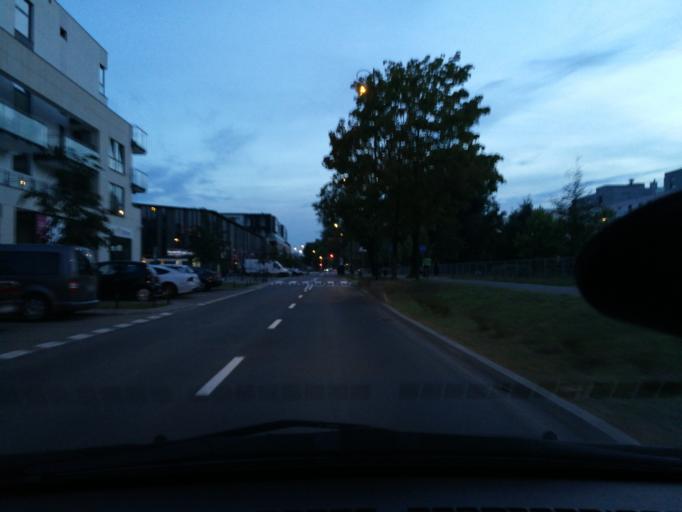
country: PL
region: Masovian Voivodeship
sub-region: Warszawa
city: Wilanow
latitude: 52.1615
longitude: 21.0754
